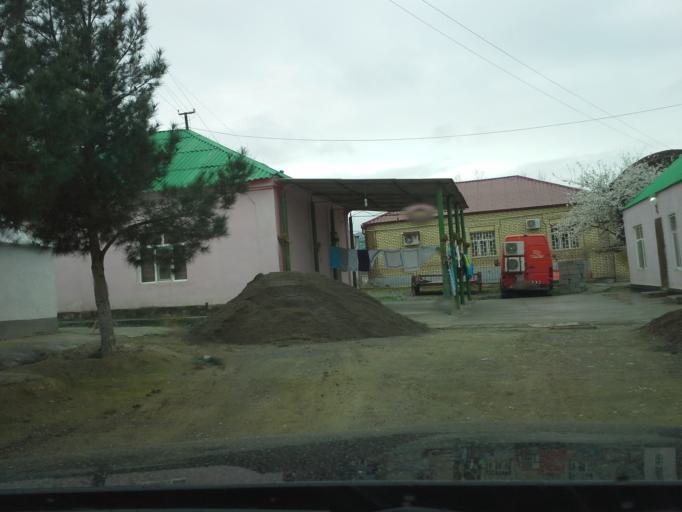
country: TM
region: Ahal
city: Abadan
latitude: 37.9592
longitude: 58.2277
